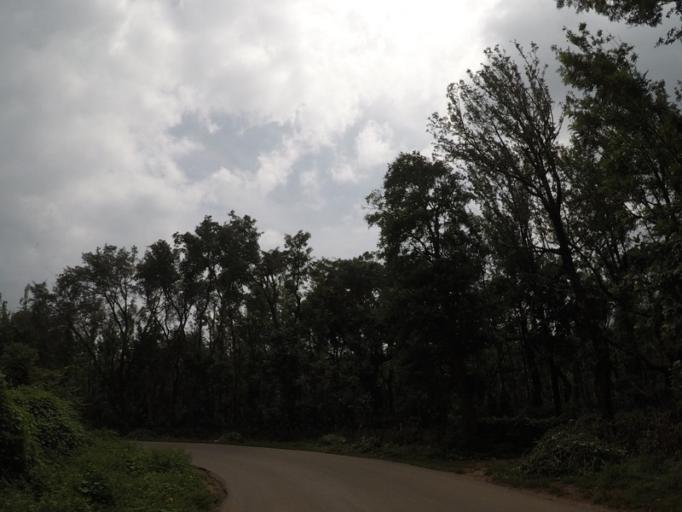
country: IN
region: Karnataka
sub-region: Chikmagalur
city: Chikmagalur
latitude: 13.4528
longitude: 75.7994
